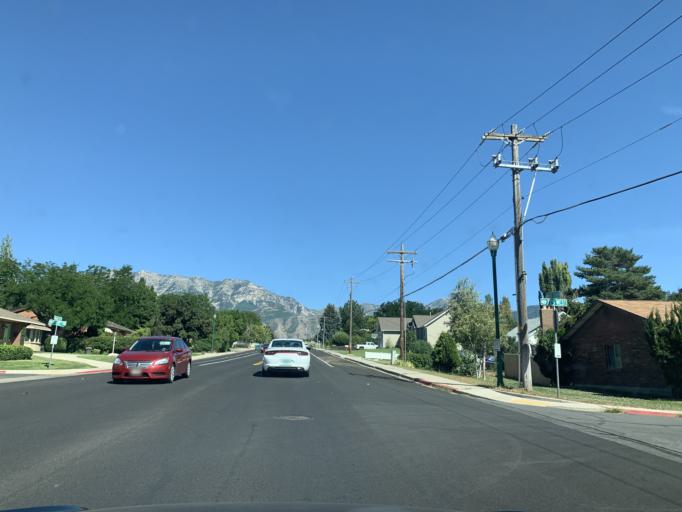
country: US
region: Utah
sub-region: Utah County
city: Orem
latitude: 40.2827
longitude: -111.7123
